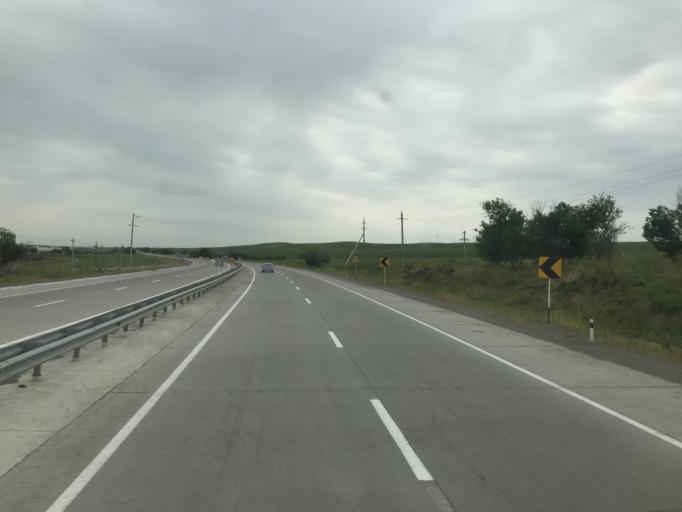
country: KZ
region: Ongtustik Qazaqstan
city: Qazyqurt
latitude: 41.8631
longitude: 69.4119
